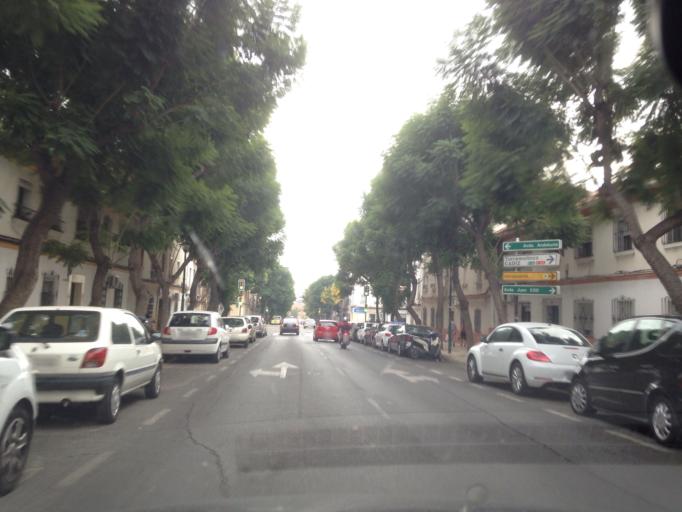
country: ES
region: Andalusia
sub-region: Provincia de Malaga
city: Malaga
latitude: 36.7165
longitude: -4.4457
